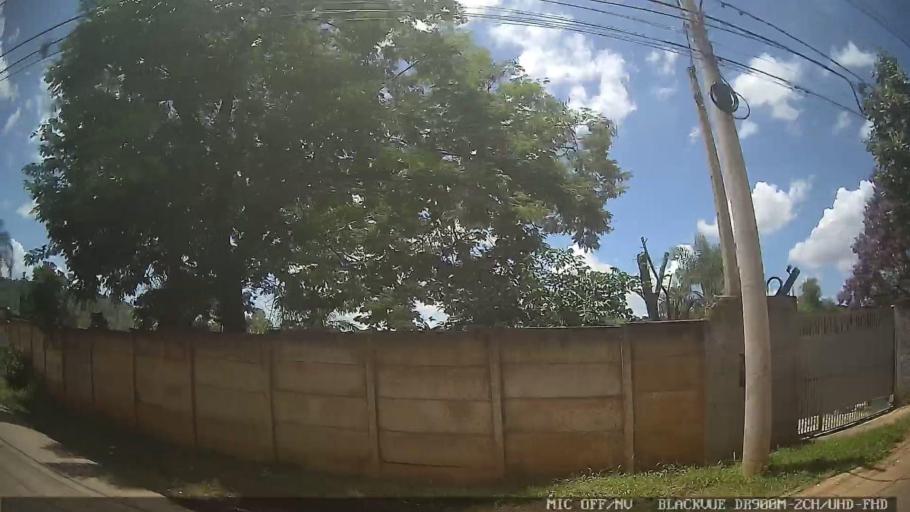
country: BR
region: Sao Paulo
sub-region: Atibaia
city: Atibaia
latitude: -23.0600
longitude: -46.5069
